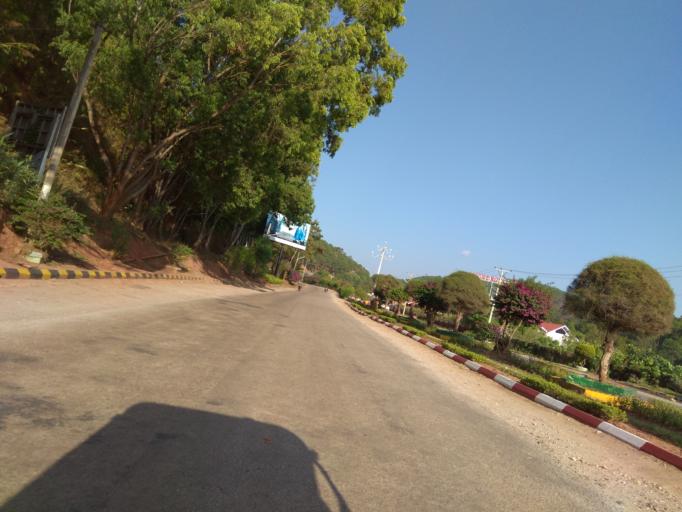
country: MM
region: Mandalay
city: Yamethin
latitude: 20.6362
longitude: 96.5708
